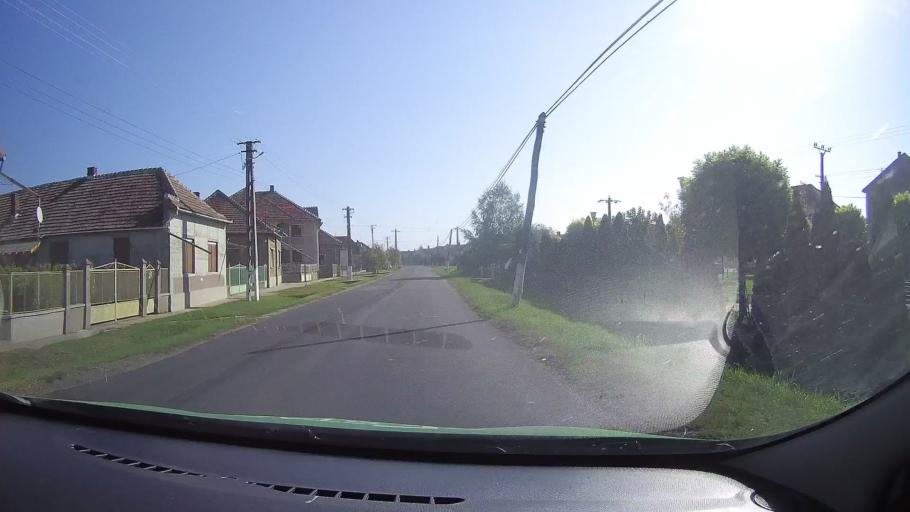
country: RO
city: Foieni
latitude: 47.6971
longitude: 22.3855
